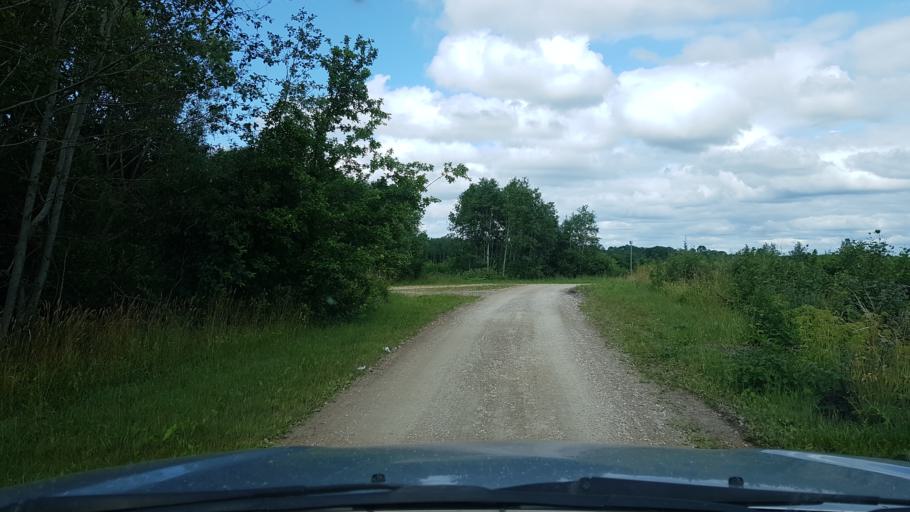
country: EE
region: Ida-Virumaa
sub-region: Narva-Joesuu linn
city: Narva-Joesuu
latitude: 59.3691
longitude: 27.9276
